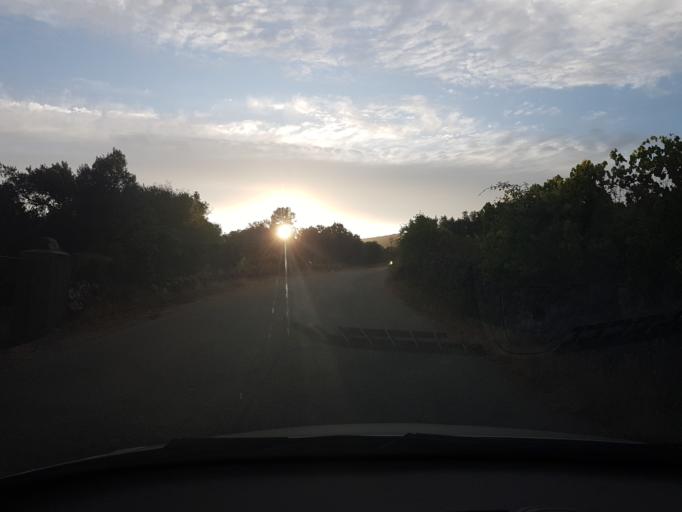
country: IT
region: Sardinia
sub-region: Provincia di Oristano
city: Seneghe
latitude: 40.0986
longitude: 8.6223
